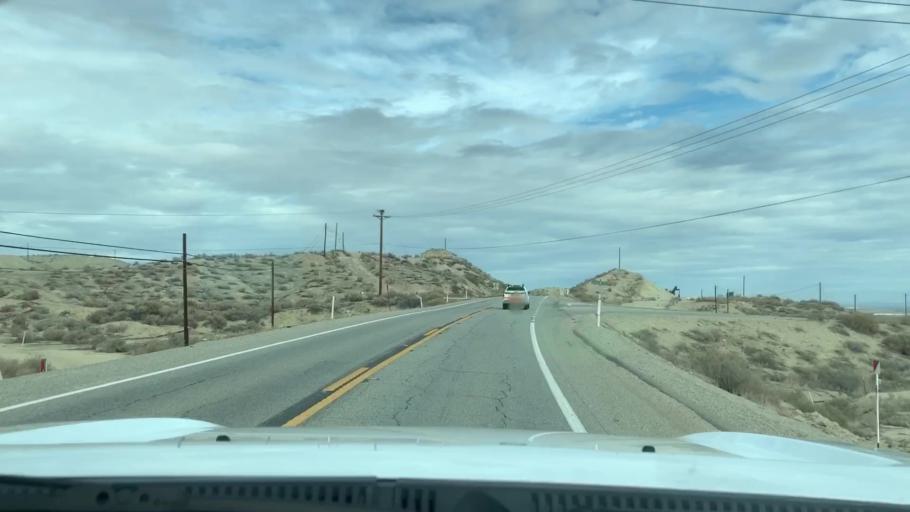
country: US
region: California
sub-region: Kern County
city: Maricopa
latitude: 35.0766
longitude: -119.4018
